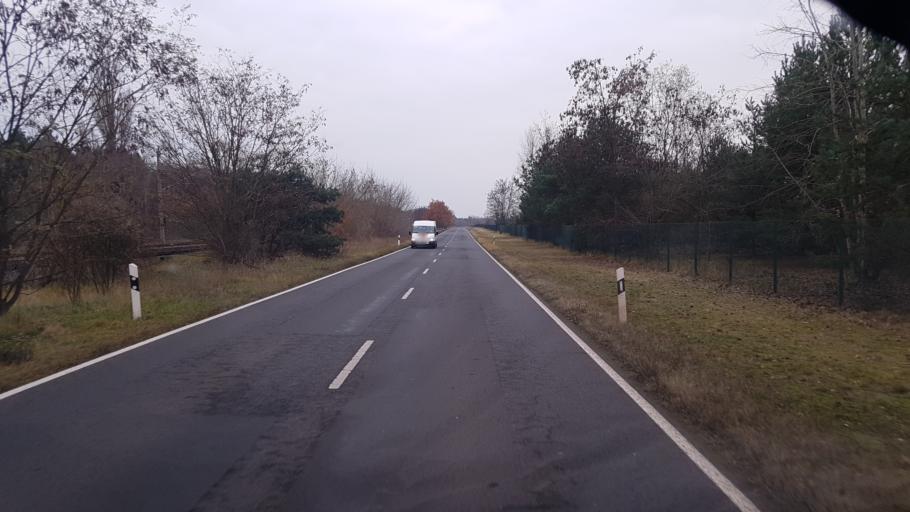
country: DE
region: Brandenburg
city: Eisenhuettenstadt
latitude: 52.1654
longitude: 14.6503
